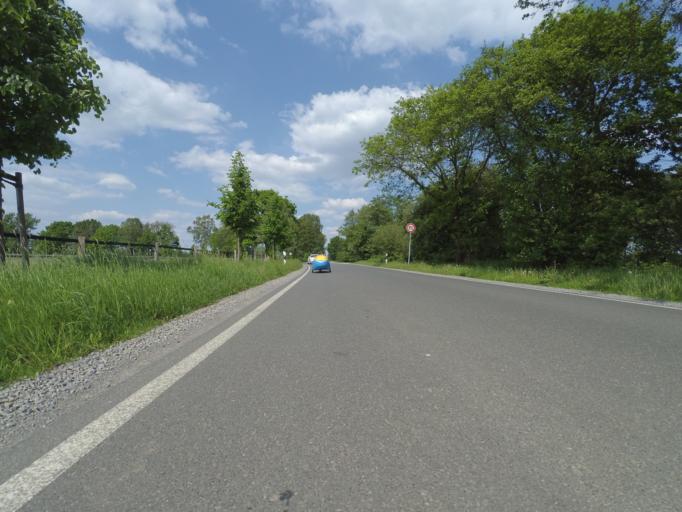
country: DE
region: Lower Saxony
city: Haenigsen
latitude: 52.5041
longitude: 10.0600
